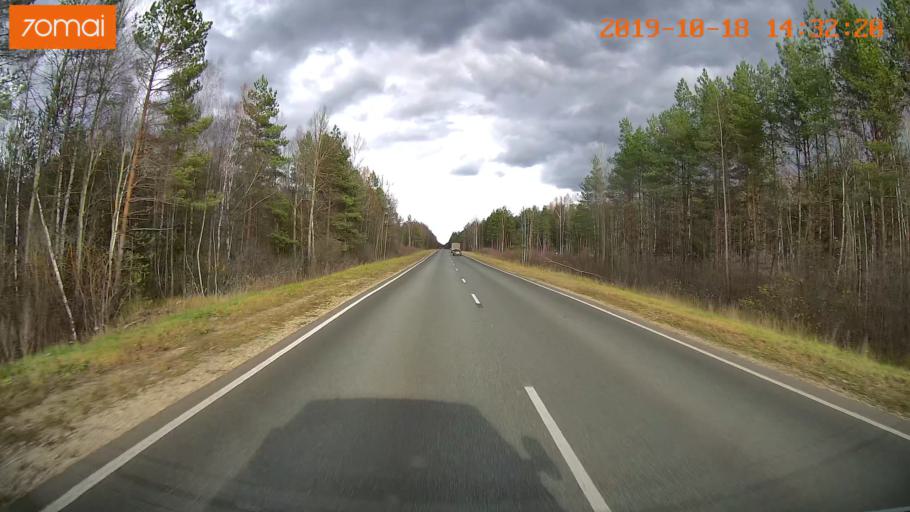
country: RU
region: Rjazan
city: Tuma
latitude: 55.1904
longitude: 40.5781
